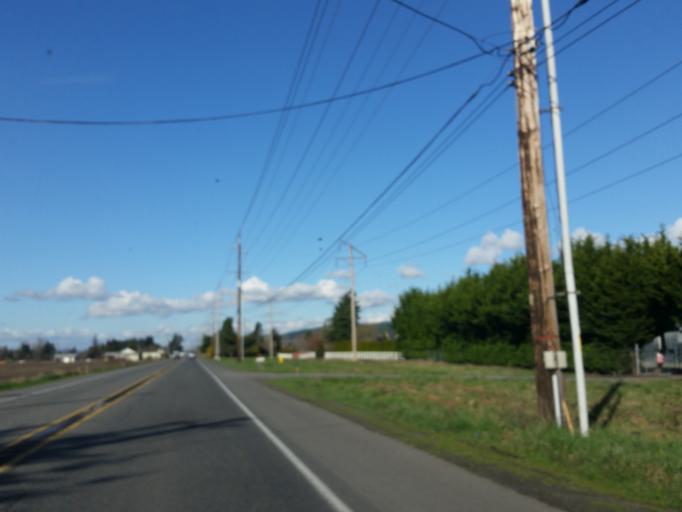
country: US
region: Washington
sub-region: Pierce County
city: Alderton
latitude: 47.1733
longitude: -122.2294
